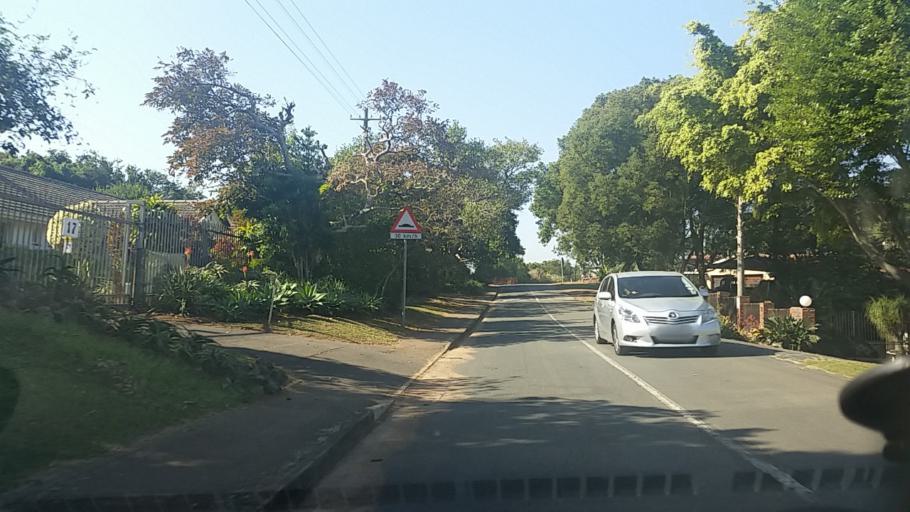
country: ZA
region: KwaZulu-Natal
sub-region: eThekwini Metropolitan Municipality
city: Berea
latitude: -29.8438
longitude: 30.9081
